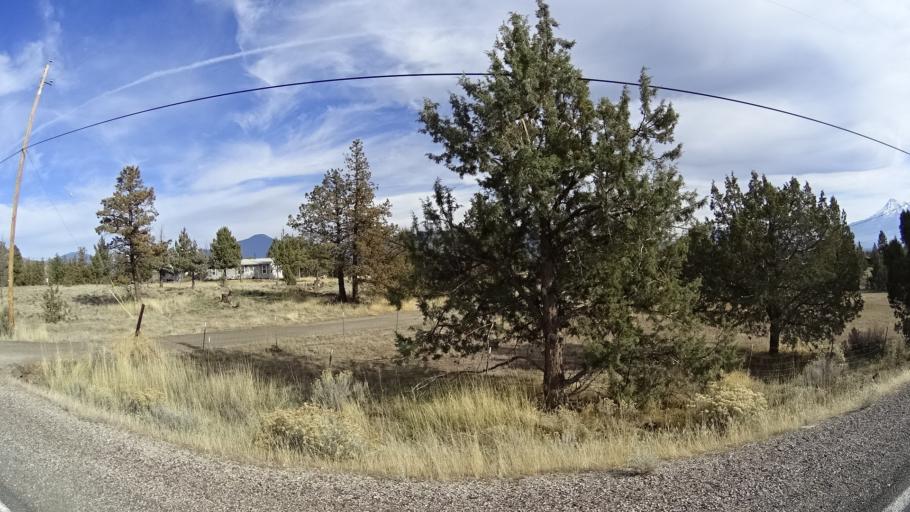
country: US
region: California
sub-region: Siskiyou County
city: Montague
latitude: 41.6471
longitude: -122.3987
